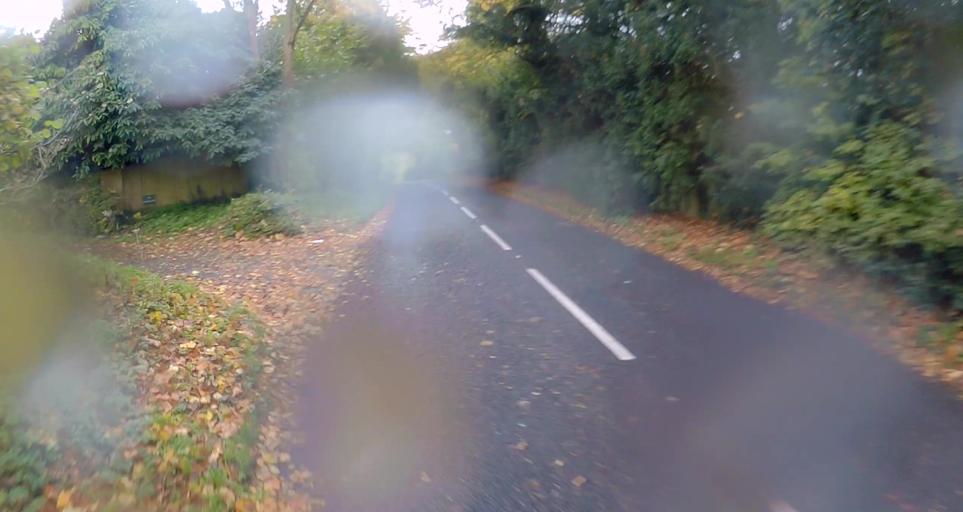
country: GB
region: England
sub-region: Hampshire
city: Kings Worthy
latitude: 51.1316
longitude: -1.1889
